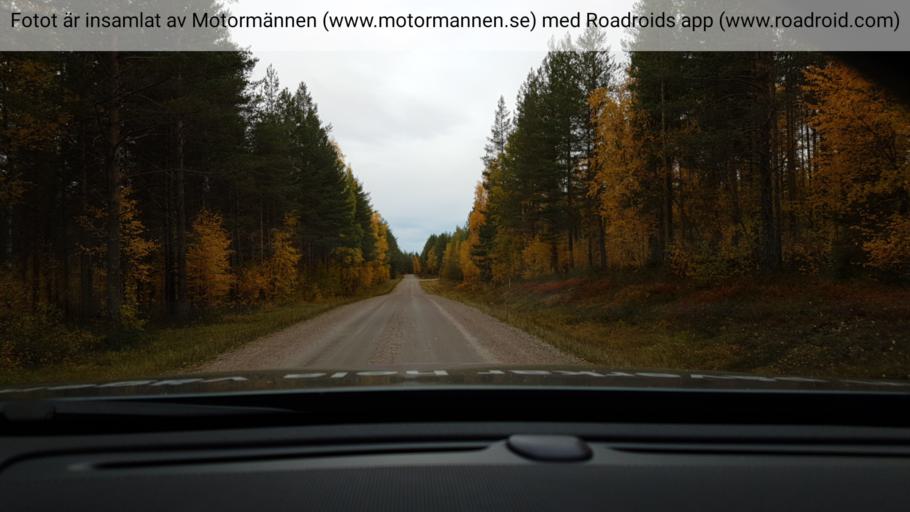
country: SE
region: Norrbotten
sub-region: Overkalix Kommun
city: OEverkalix
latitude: 66.2753
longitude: 22.9867
